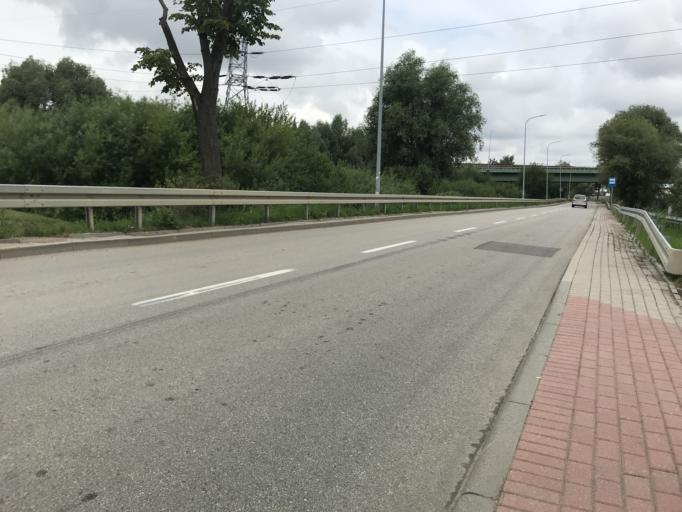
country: PL
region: Warmian-Masurian Voivodeship
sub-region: Powiat elblaski
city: Elblag
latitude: 54.1709
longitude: 19.3870
